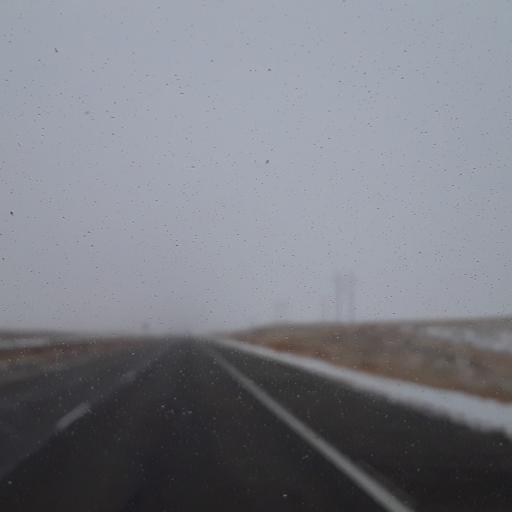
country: US
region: Nebraska
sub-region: Cheyenne County
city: Sidney
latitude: 40.7959
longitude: -102.8781
